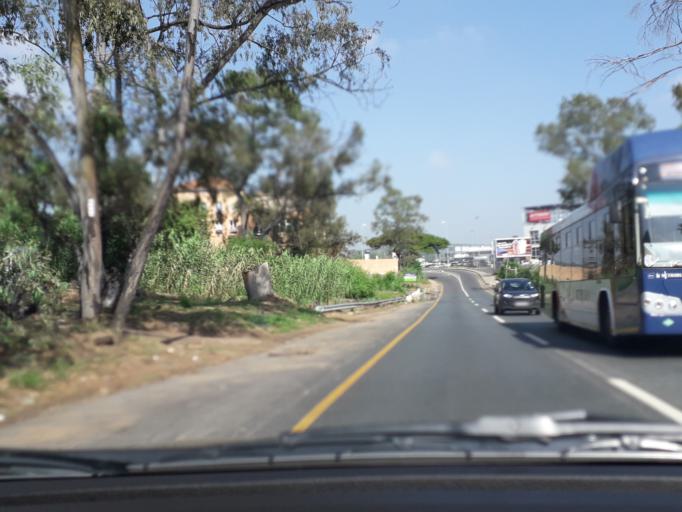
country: ZA
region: Gauteng
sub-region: City of Johannesburg Metropolitan Municipality
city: Midrand
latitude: -26.0381
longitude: 28.0651
